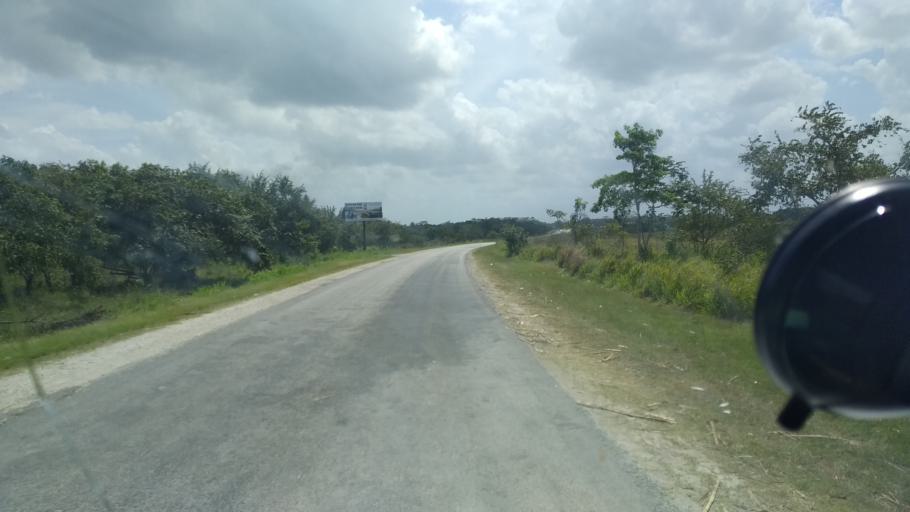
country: BZ
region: Orange Walk
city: Orange Walk
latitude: 18.0531
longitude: -88.5652
